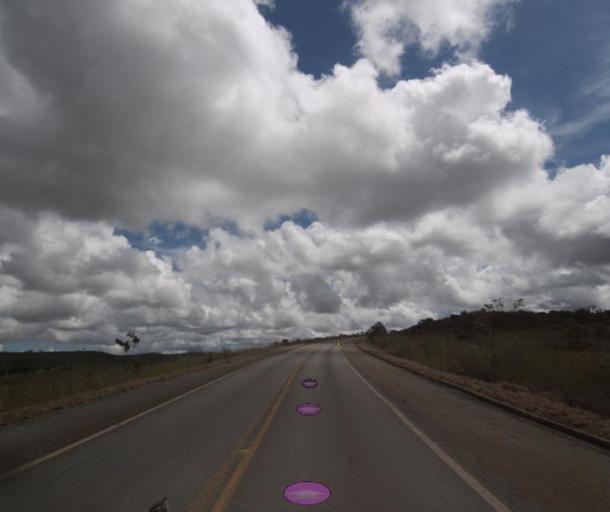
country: BR
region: Goias
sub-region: Pirenopolis
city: Pirenopolis
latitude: -15.7680
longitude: -48.7174
